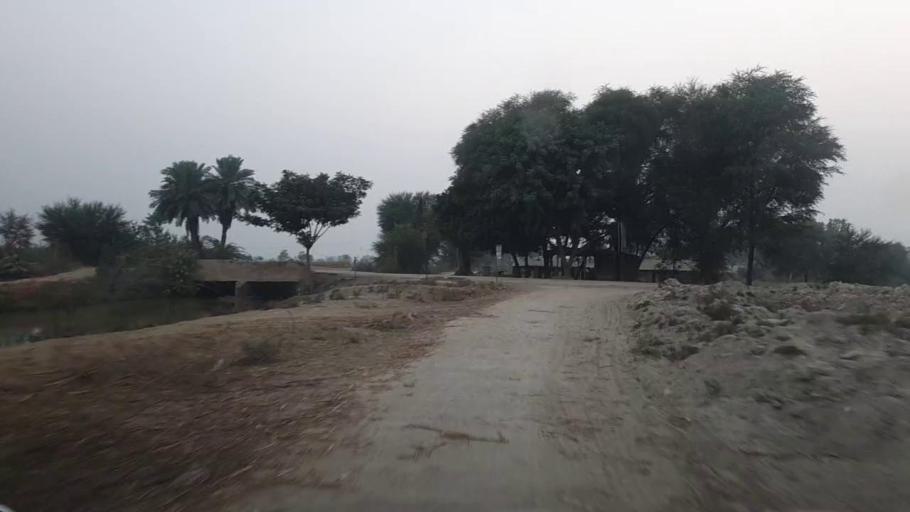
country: PK
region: Sindh
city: Karaundi
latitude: 26.9406
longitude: 68.4454
